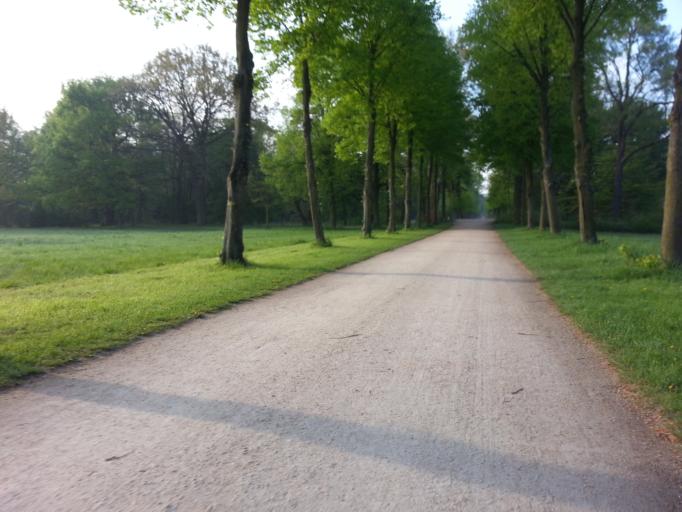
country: DE
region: Berlin
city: Charlottenburg-Nord
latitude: 52.5259
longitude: 13.2901
